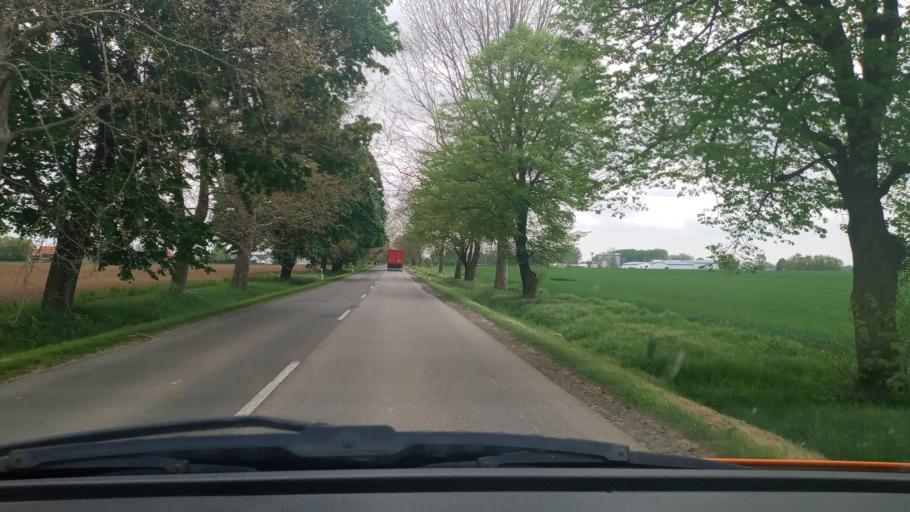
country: HU
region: Baranya
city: Boly
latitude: 45.9872
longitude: 18.5243
